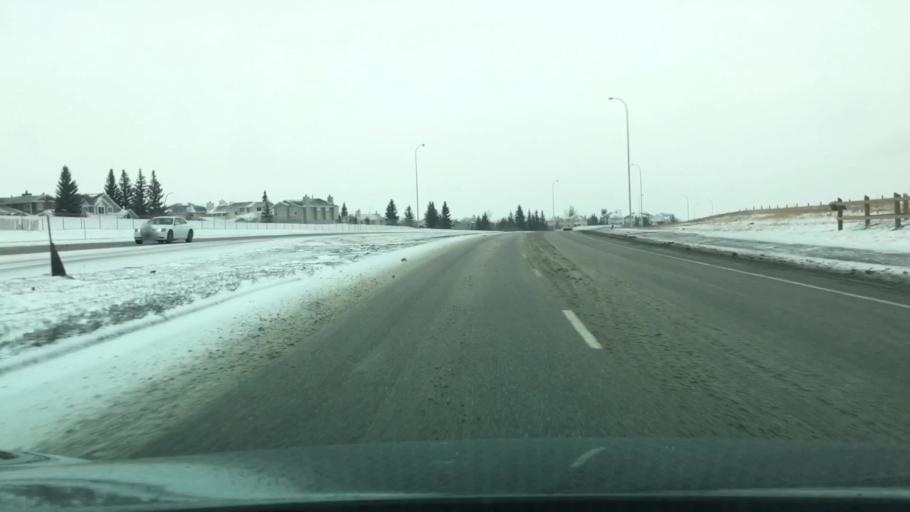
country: CA
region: Alberta
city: Calgary
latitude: 51.1272
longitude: -114.1327
